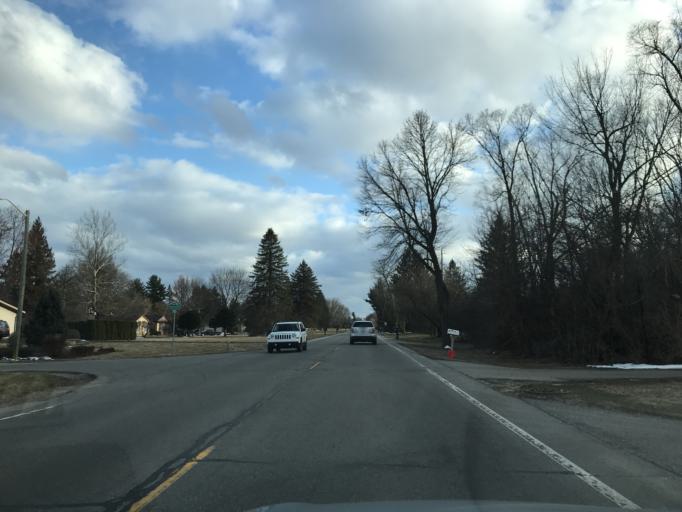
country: US
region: Michigan
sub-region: Oakland County
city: Farmington
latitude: 42.4633
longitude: -83.3179
